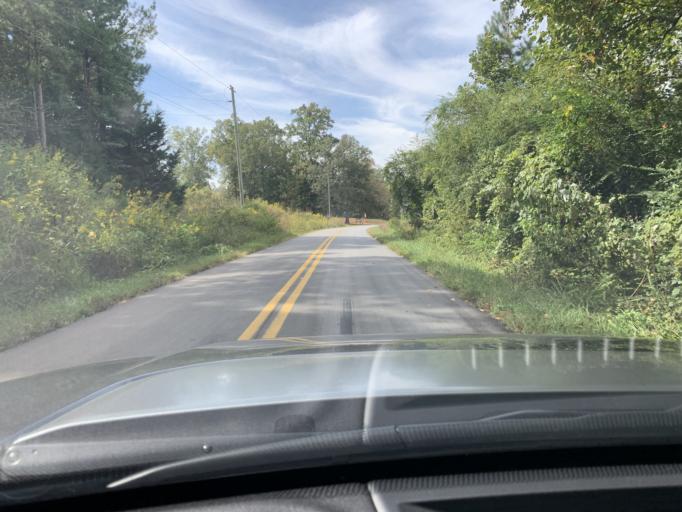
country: US
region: Georgia
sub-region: Polk County
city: Cedartown
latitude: 33.9487
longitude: -85.3571
